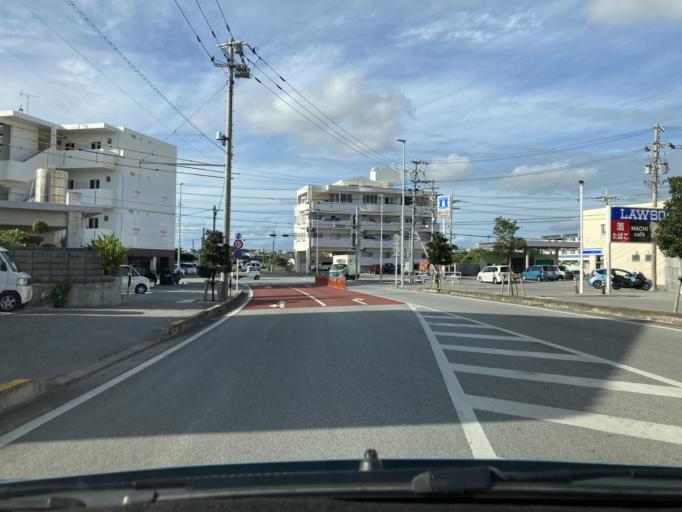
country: JP
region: Okinawa
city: Itoman
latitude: 26.1309
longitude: 127.6835
